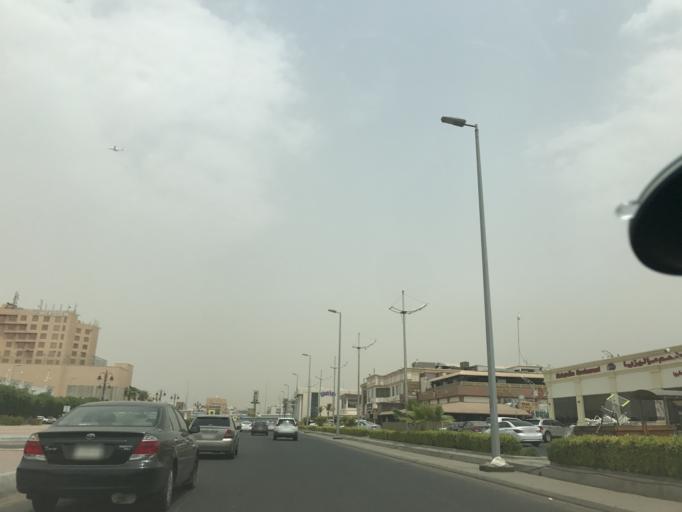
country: SA
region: Makkah
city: Jeddah
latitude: 21.5574
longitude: 39.1701
